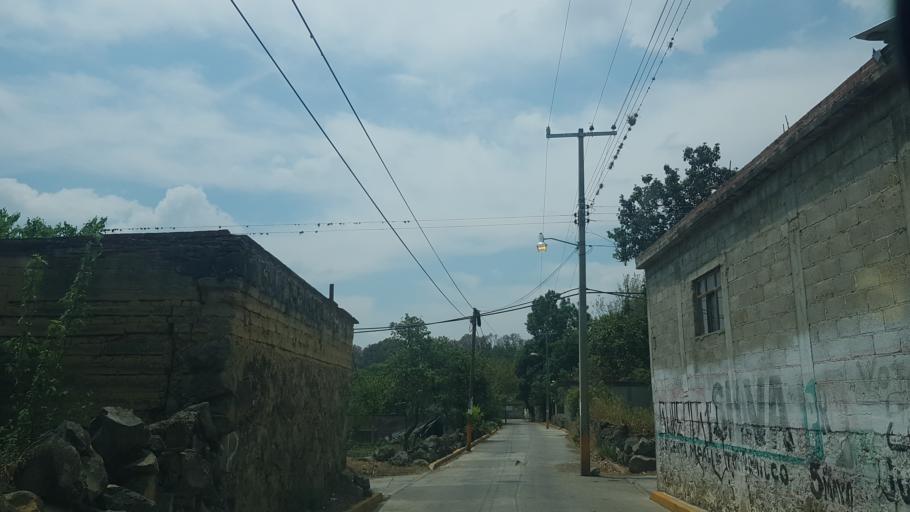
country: MX
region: Puebla
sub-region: Tochimilco
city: La Magdalena Yancuitlalpan
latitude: 18.8890
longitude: -98.6108
